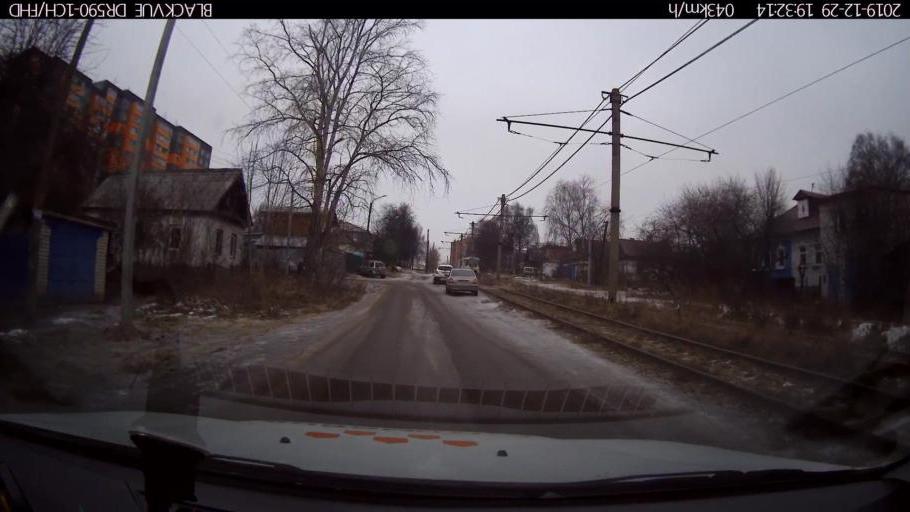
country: RU
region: Nizjnij Novgorod
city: Nizhniy Novgorod
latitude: 56.2977
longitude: 44.0304
